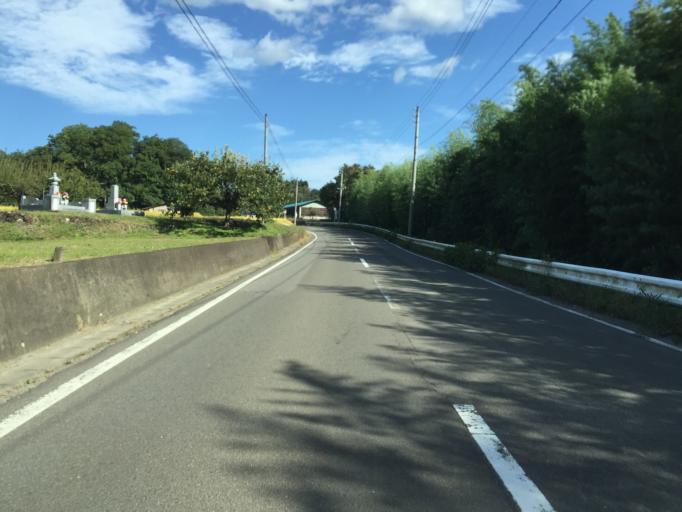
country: JP
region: Fukushima
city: Yanagawamachi-saiwaicho
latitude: 37.8584
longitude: 140.6213
